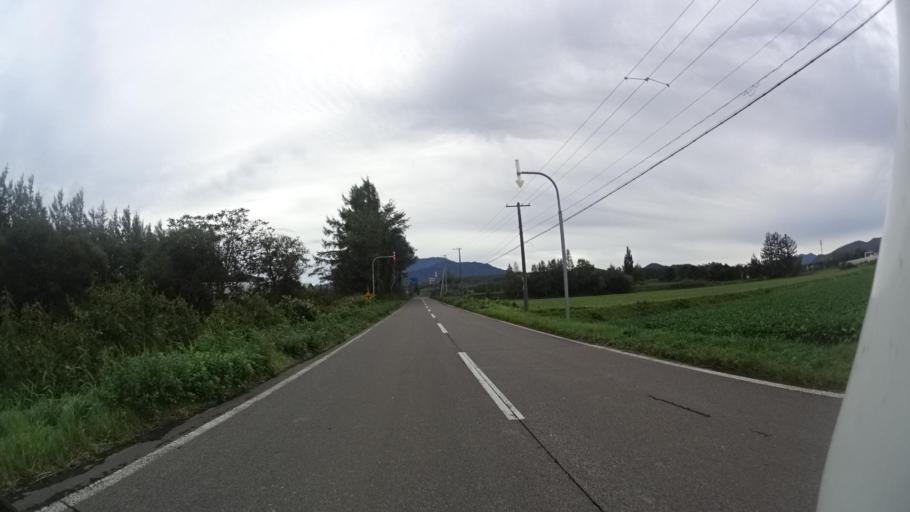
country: JP
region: Hokkaido
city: Shibetsu
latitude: 43.8743
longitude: 144.7440
